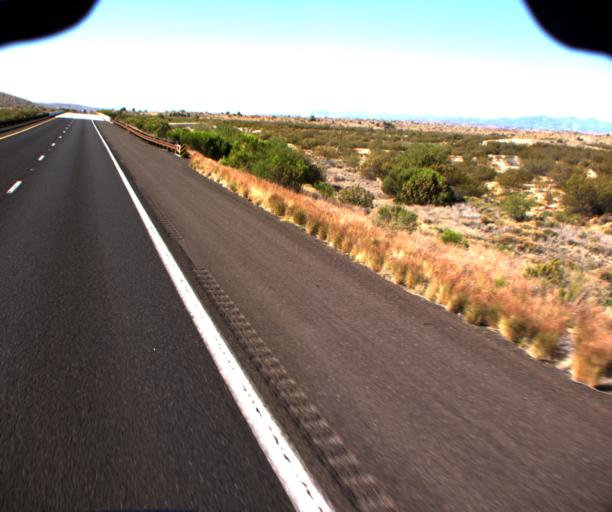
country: US
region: Arizona
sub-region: Mohave County
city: Kingman
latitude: 35.0393
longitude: -113.6652
